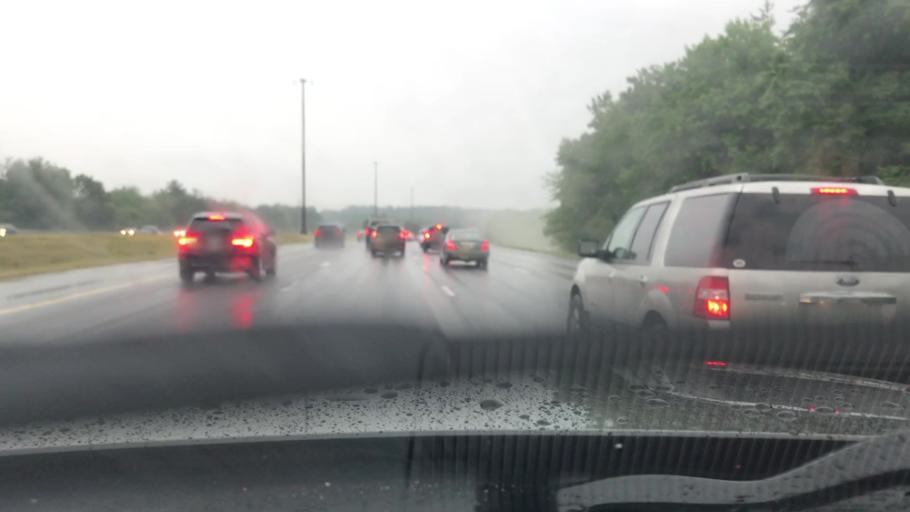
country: US
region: New Hampshire
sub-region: Rockingham County
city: Greenland
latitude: 43.0512
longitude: -70.8110
